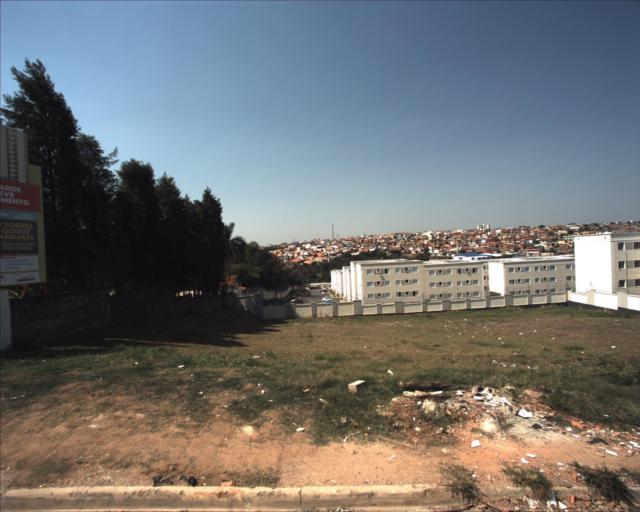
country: BR
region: Sao Paulo
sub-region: Sorocaba
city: Sorocaba
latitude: -23.4512
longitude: -47.4965
